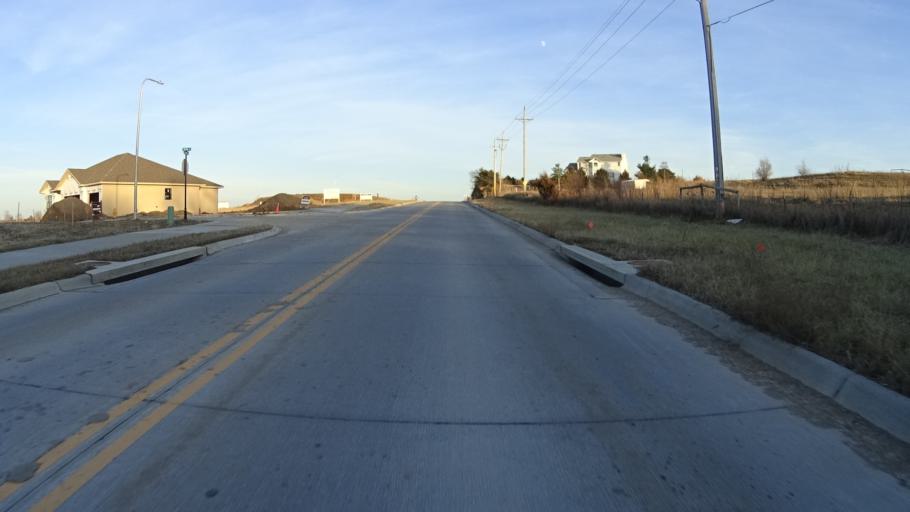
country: US
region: Nebraska
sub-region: Sarpy County
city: Papillion
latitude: 41.1327
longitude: -96.0804
